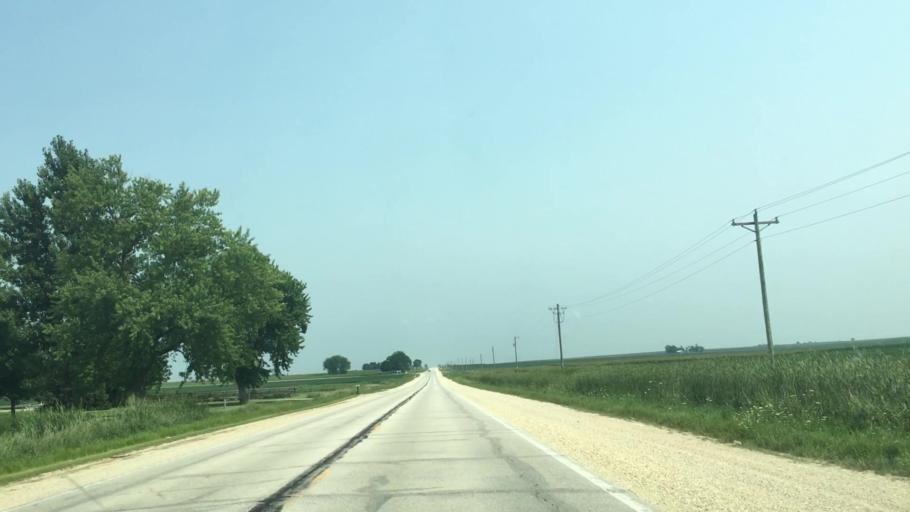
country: US
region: Iowa
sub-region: Fayette County
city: Oelwein
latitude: 42.6874
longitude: -91.8134
